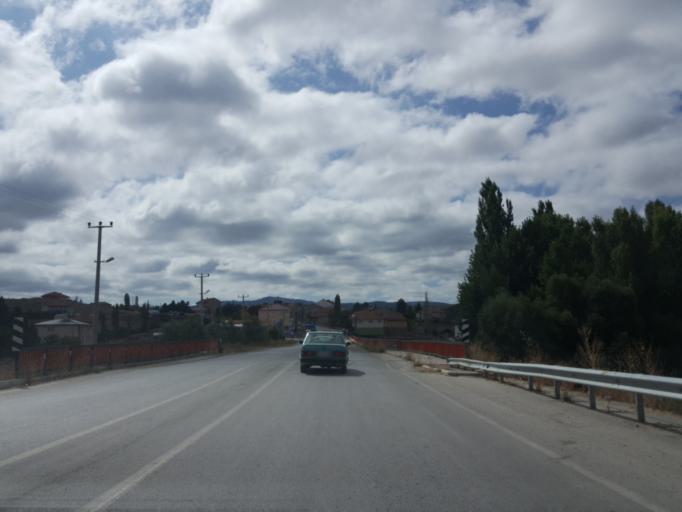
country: TR
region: Sivas
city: Yavu
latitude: 39.7970
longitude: 36.2030
